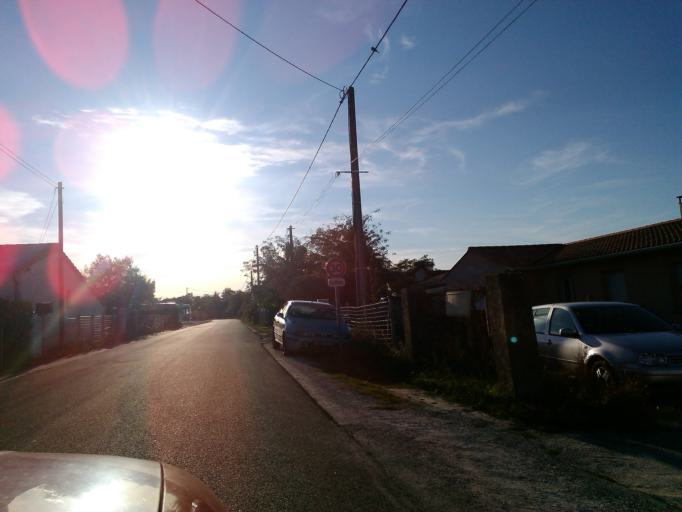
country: FR
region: Aquitaine
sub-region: Departement de la Gironde
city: Soulac-sur-Mer
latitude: 45.4317
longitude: -1.0385
